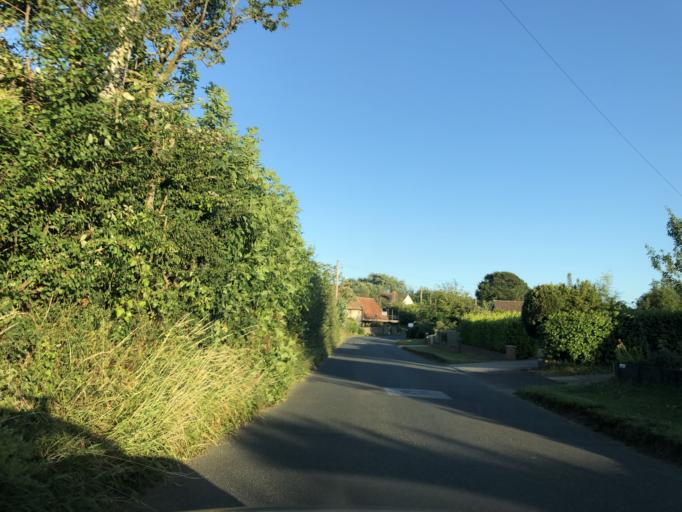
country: GB
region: England
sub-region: Isle of Wight
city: Chale
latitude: 50.6430
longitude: -1.3539
